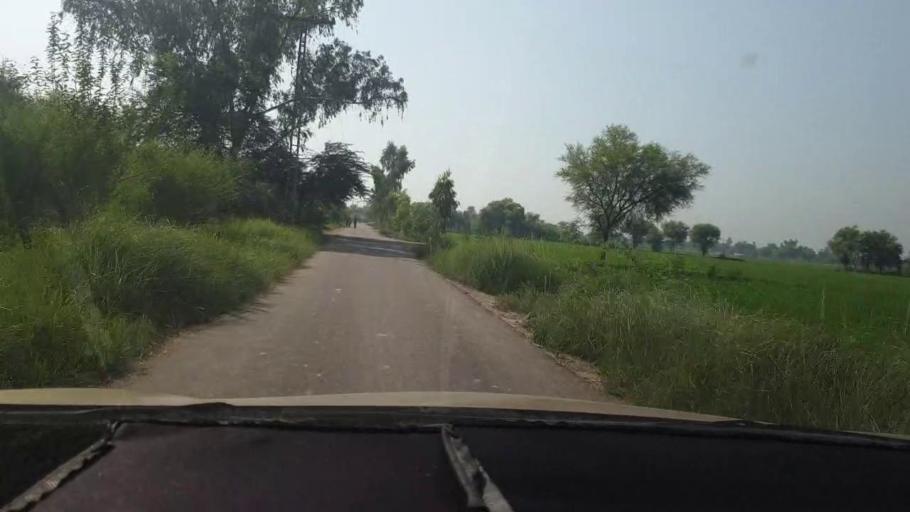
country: PK
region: Sindh
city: Kambar
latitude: 27.5795
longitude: 68.0735
